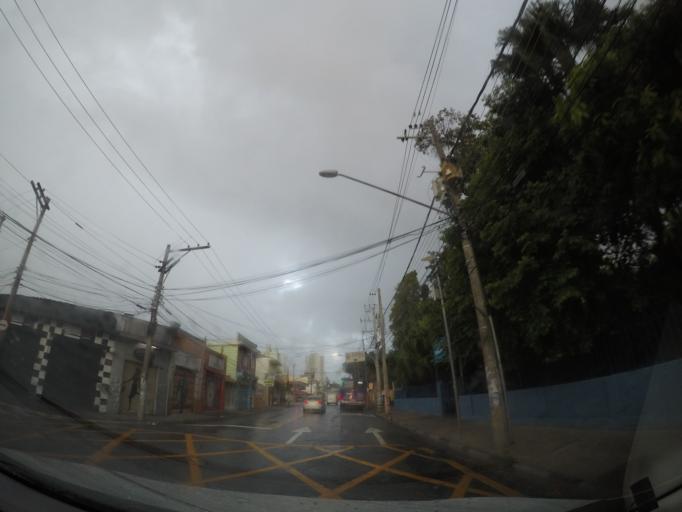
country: BR
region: Sao Paulo
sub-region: Guarulhos
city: Guarulhos
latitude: -23.4645
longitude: -46.5512
